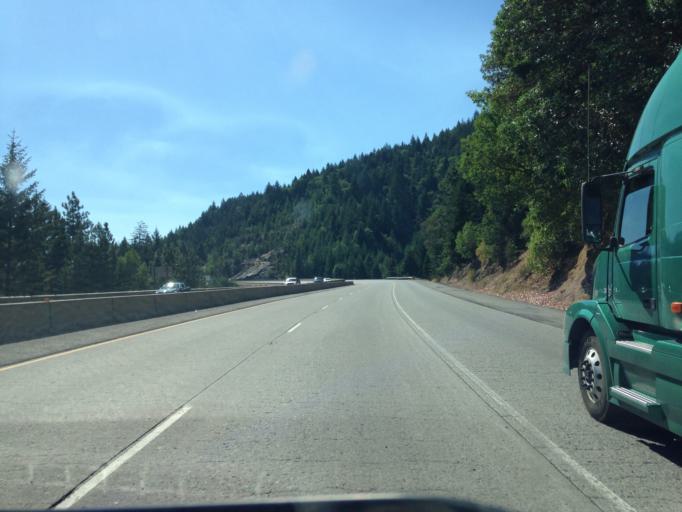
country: US
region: Oregon
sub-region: Jackson County
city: Ashland
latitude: 42.1122
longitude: -122.6184
